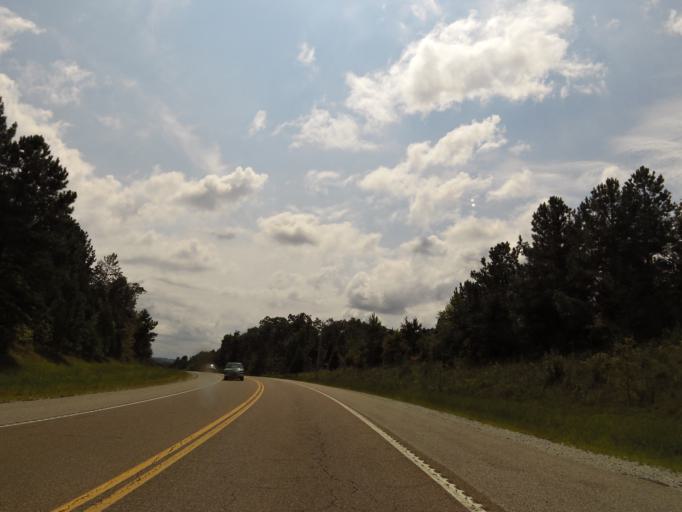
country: US
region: Tennessee
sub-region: Decatur County
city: Parsons
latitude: 35.6283
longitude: -88.0509
